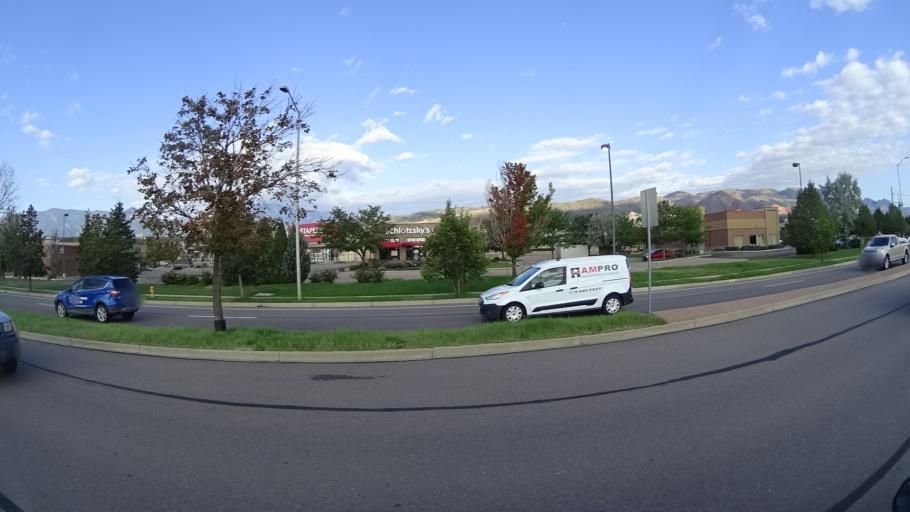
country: US
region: Colorado
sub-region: El Paso County
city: Colorado Springs
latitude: 38.8980
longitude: -104.8509
